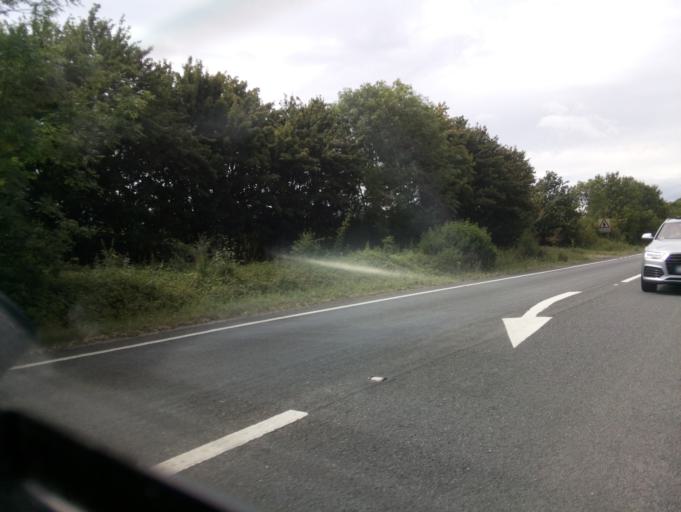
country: GB
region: England
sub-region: Somerset
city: Yeovil
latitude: 50.8927
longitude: -2.6152
